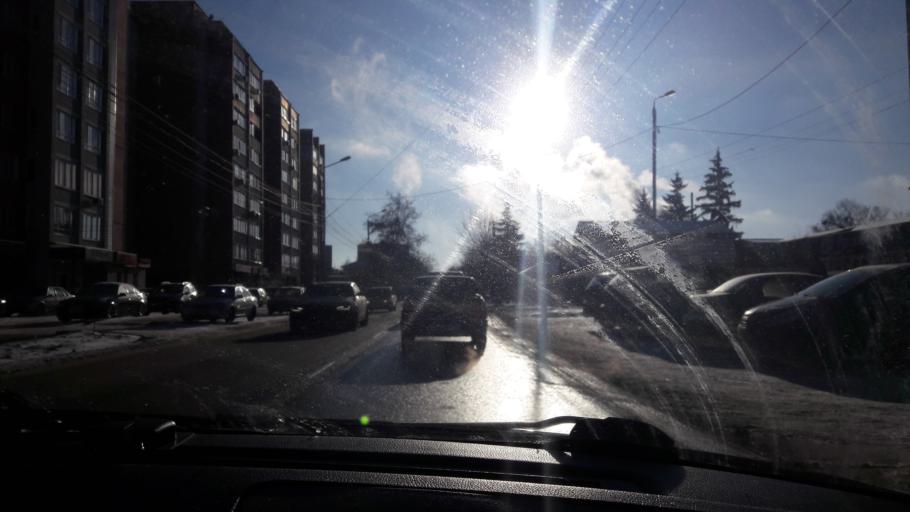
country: RU
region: Tula
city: Tula
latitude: 54.1809
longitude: 37.6291
